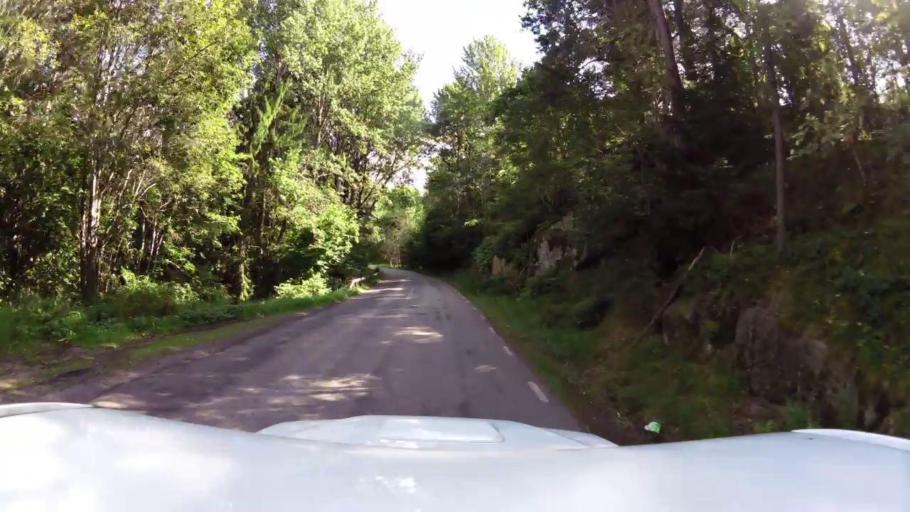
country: SE
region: OEstergoetland
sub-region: Kinda Kommun
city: Rimforsa
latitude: 58.2266
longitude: 15.7037
